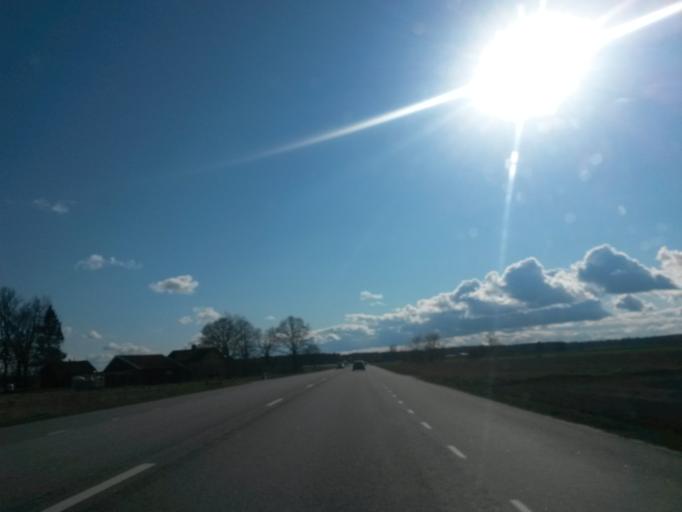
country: SE
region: Vaestra Goetaland
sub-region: Vara Kommun
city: Vara
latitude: 58.2386
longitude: 12.9369
